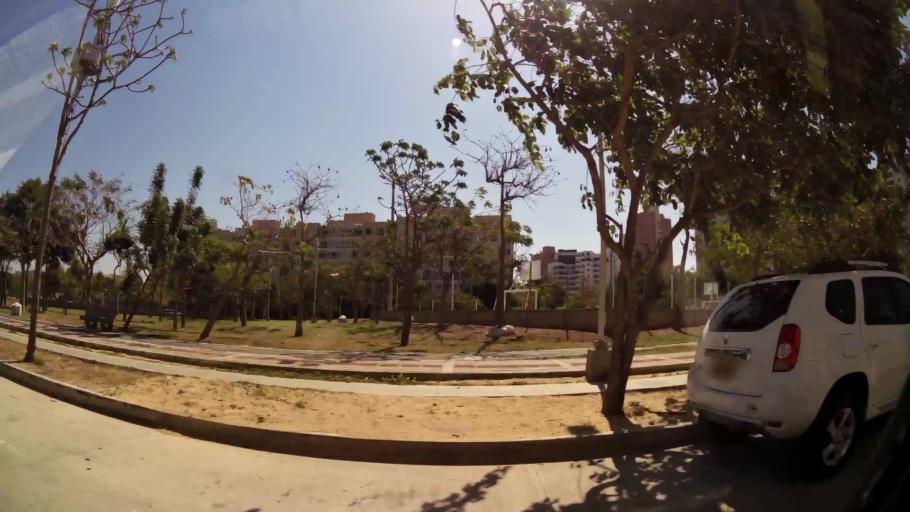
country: CO
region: Atlantico
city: Barranquilla
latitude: 11.0199
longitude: -74.8244
